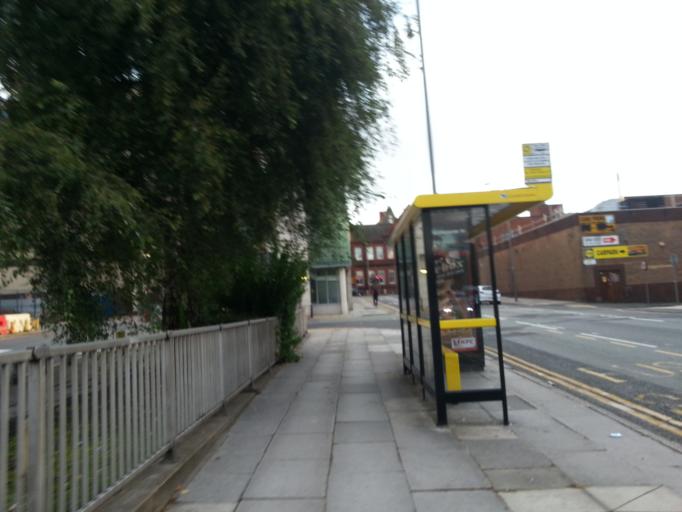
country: GB
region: England
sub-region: Liverpool
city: Liverpool
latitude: 53.4097
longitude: -2.9678
